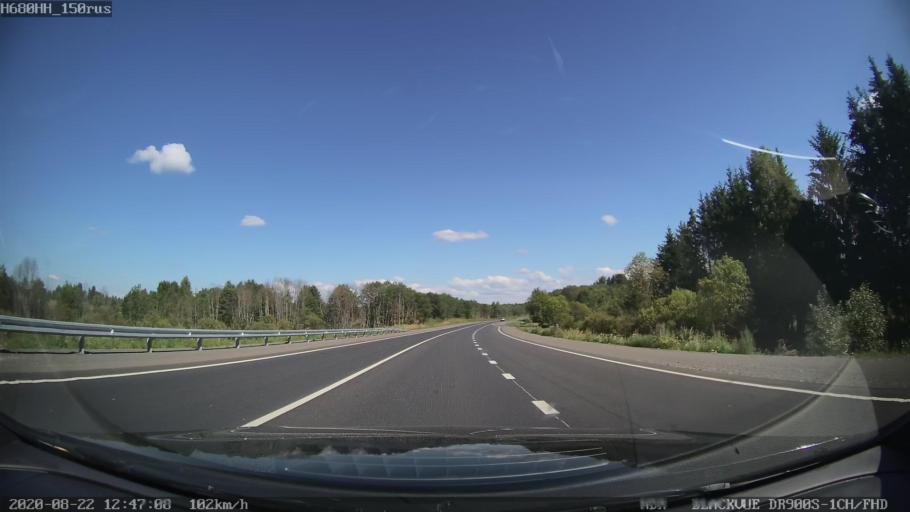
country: RU
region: Tverskaya
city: Rameshki
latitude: 57.4271
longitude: 36.1587
